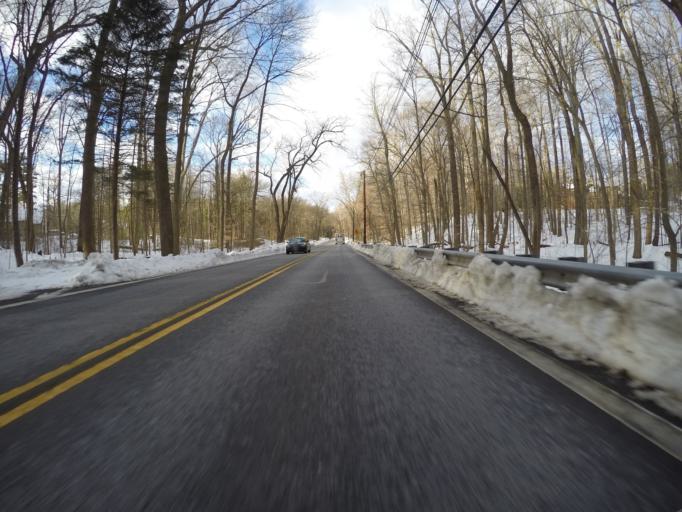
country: US
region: Maryland
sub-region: Baltimore County
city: Pikesville
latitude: 39.4004
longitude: -76.7278
